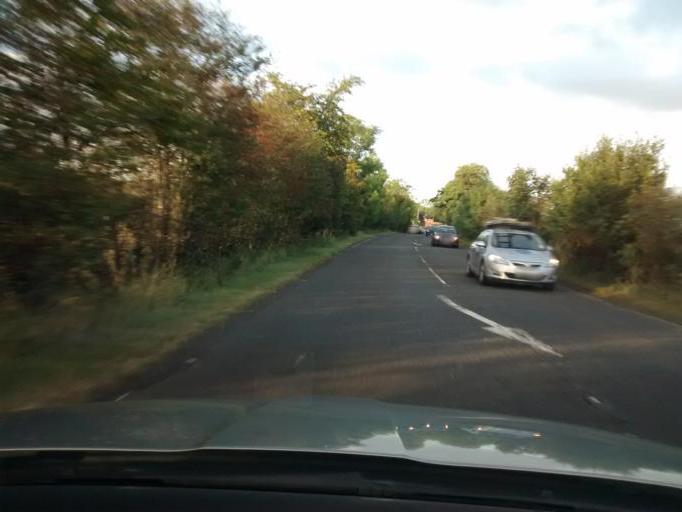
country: GB
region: Scotland
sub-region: Renfrewshire
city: Lochwinnoch
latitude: 55.7946
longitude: -4.5984
